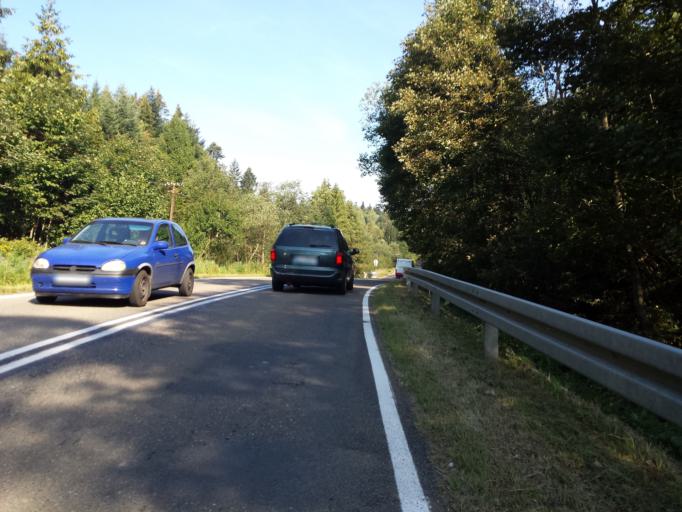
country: PL
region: Subcarpathian Voivodeship
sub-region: Powiat leski
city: Cisna
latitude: 49.2256
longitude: 22.3058
